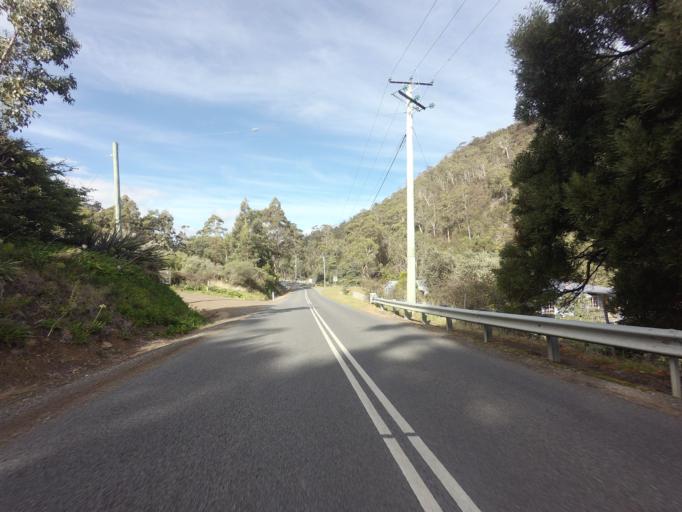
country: AU
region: Tasmania
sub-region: Clarence
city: Sandford
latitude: -43.1122
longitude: 147.7488
